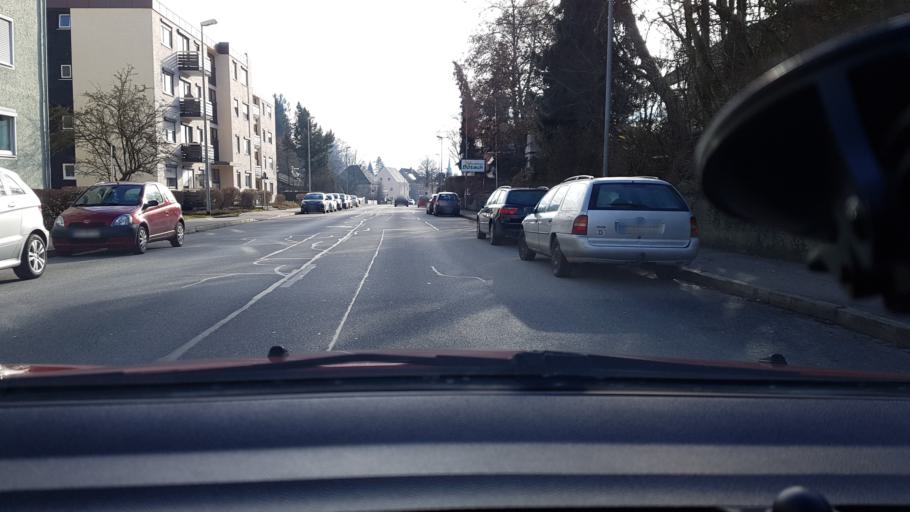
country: DE
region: Bavaria
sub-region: Lower Bavaria
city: Pfarrkirchen
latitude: 48.4386
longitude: 12.9362
